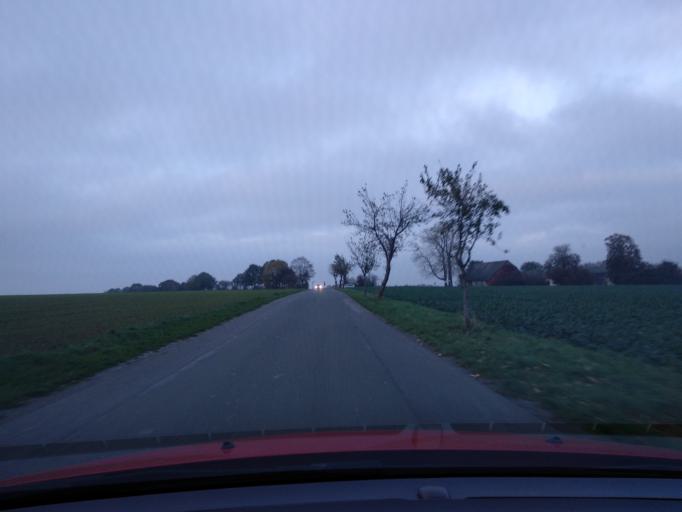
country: DE
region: North Rhine-Westphalia
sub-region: Regierungsbezirk Detmold
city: Paderborn
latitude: 51.6778
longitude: 8.7699
